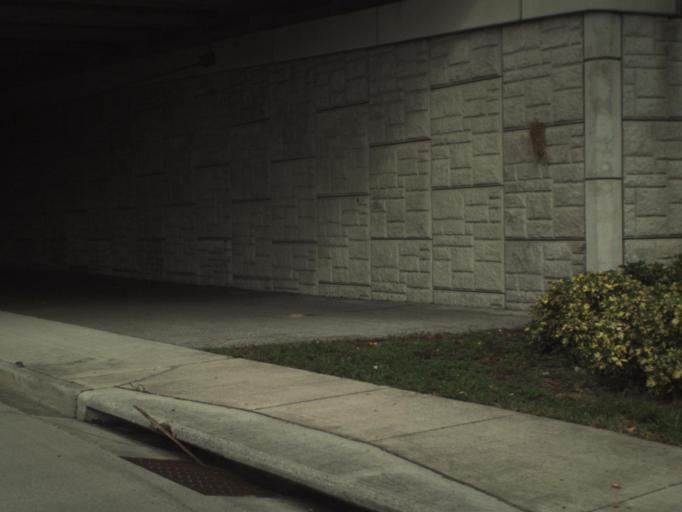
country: US
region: Florida
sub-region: Palm Beach County
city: Schall Circle
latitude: 26.7194
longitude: -80.0895
